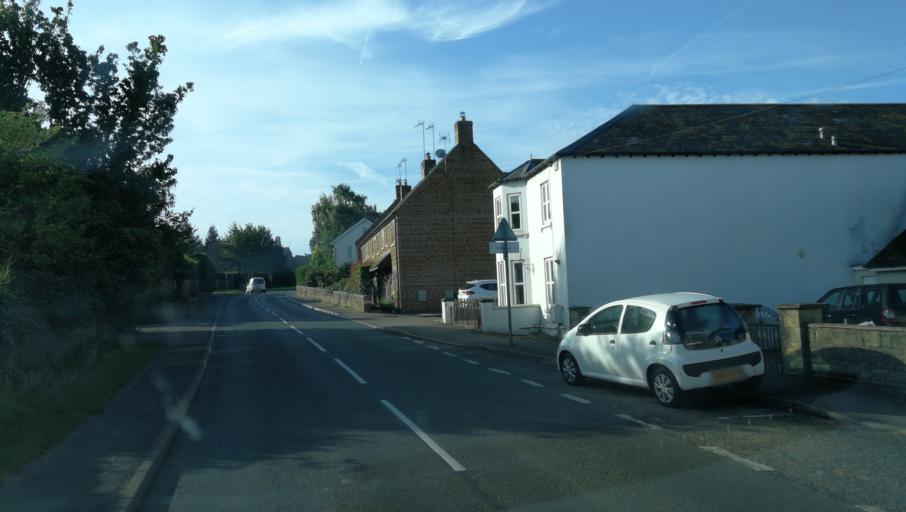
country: GB
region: England
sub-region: Oxfordshire
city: Bloxham
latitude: 52.0155
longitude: -1.3759
